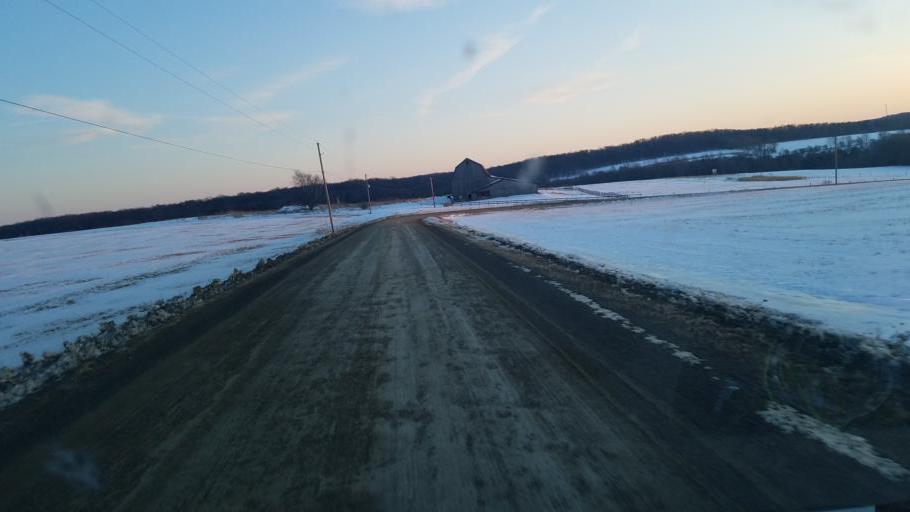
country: US
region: New York
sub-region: Allegany County
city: Andover
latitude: 42.0079
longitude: -77.7055
